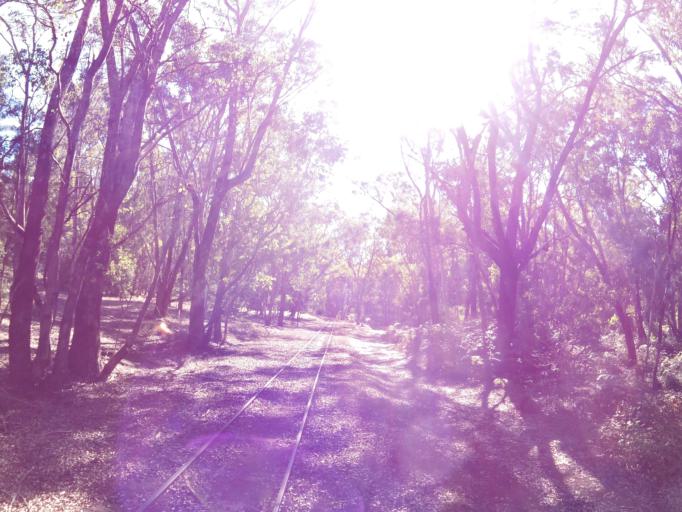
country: AU
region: Western Australia
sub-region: Waroona
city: Waroona
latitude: -32.7140
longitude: 116.0929
